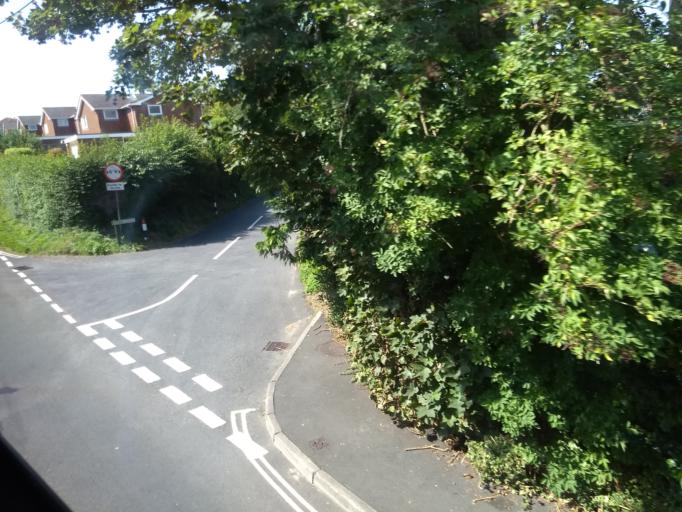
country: GB
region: England
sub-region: Isle of Wight
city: Totland
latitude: 50.6763
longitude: -1.5453
